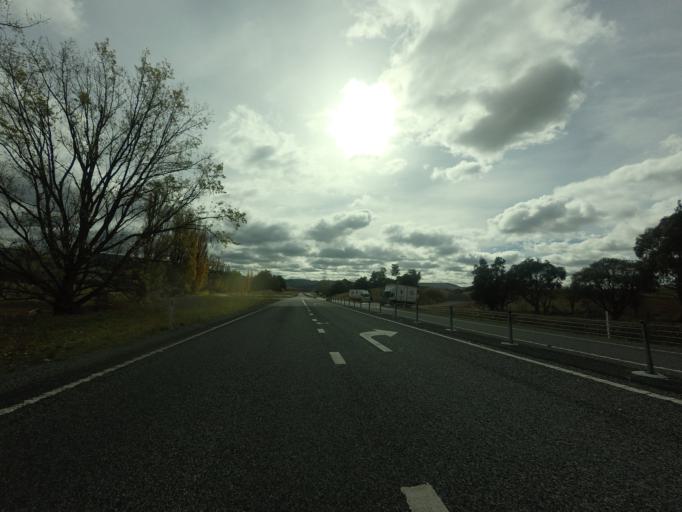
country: AU
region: Tasmania
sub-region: Brighton
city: Bridgewater
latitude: -42.4864
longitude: 147.1823
